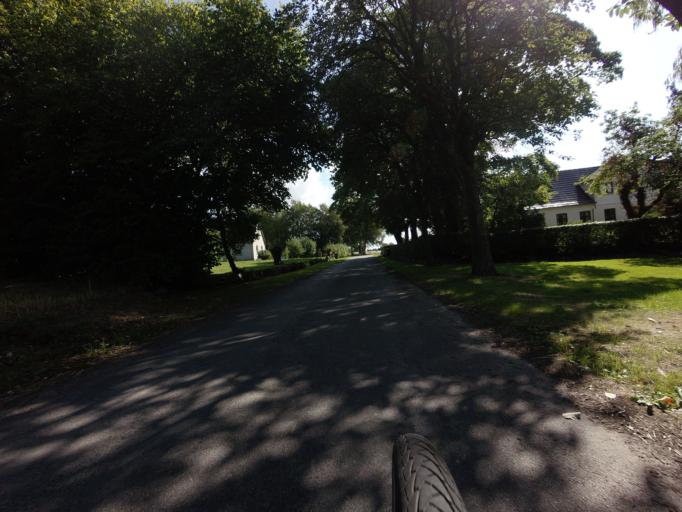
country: DK
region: Zealand
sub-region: Vordingborg Kommune
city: Stege
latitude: 54.9761
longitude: 12.3371
